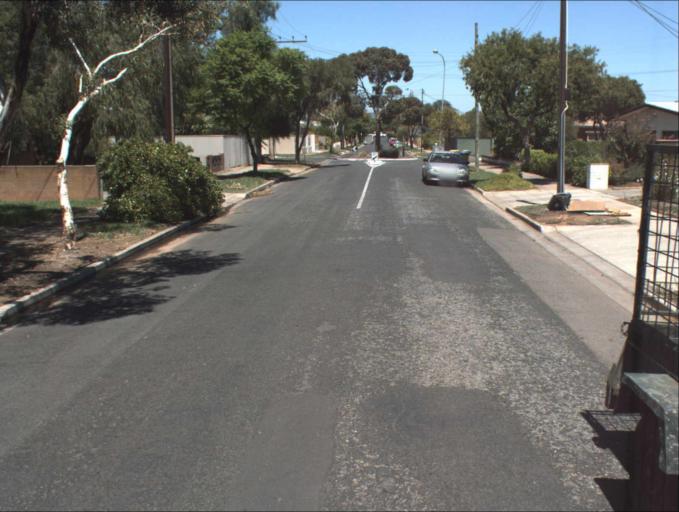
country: AU
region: South Australia
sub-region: Port Adelaide Enfield
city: Klemzig
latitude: -34.8704
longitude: 138.6159
